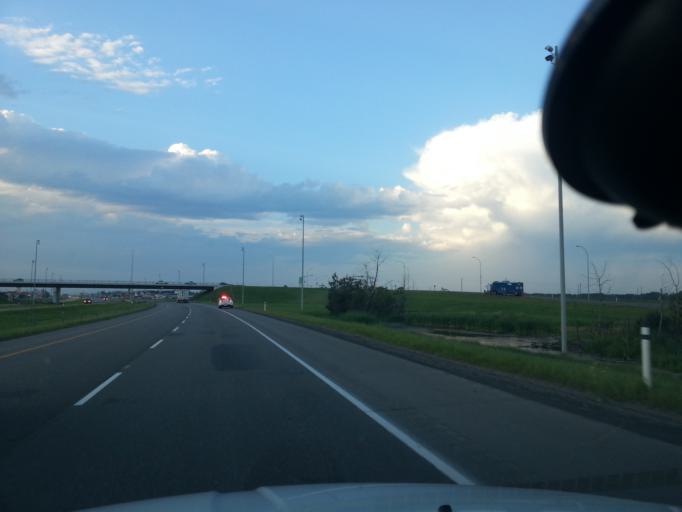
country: CA
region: Alberta
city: Red Deer
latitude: 52.1987
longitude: -113.8146
